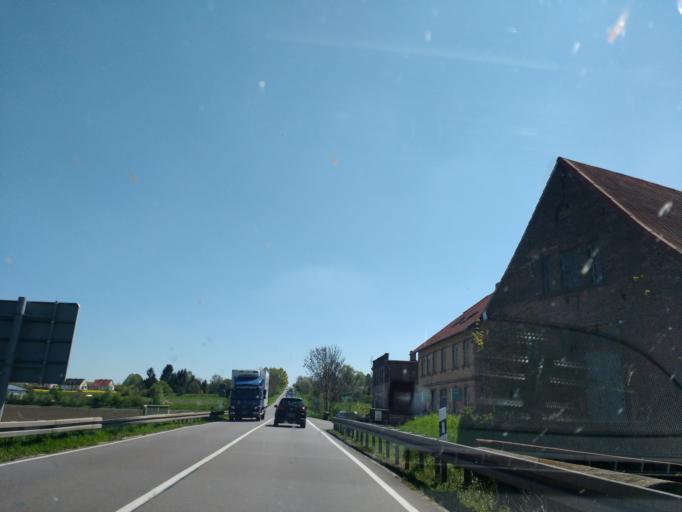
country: DE
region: Saxony-Anhalt
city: Deuben
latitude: 51.1303
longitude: 12.0570
